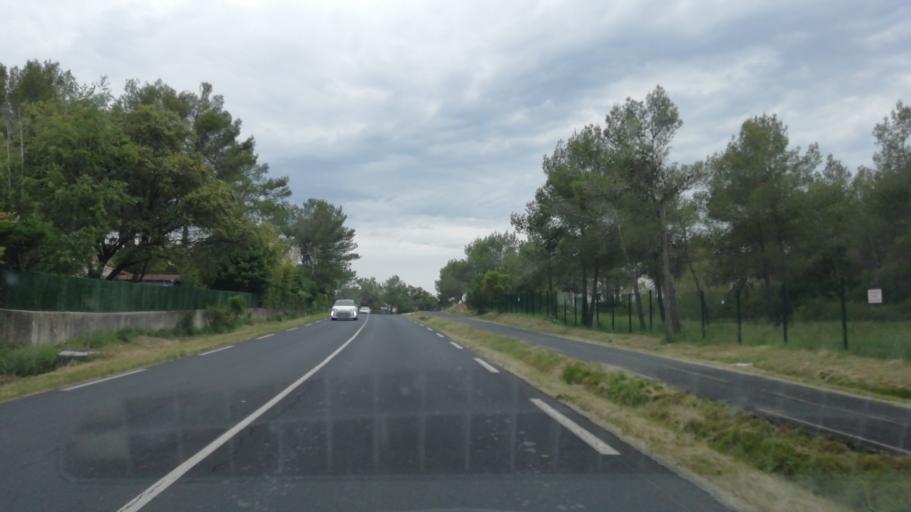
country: FR
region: Languedoc-Roussillon
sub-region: Departement de l'Herault
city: Saint-Clement-de-Riviere
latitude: 43.7056
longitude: 3.8331
